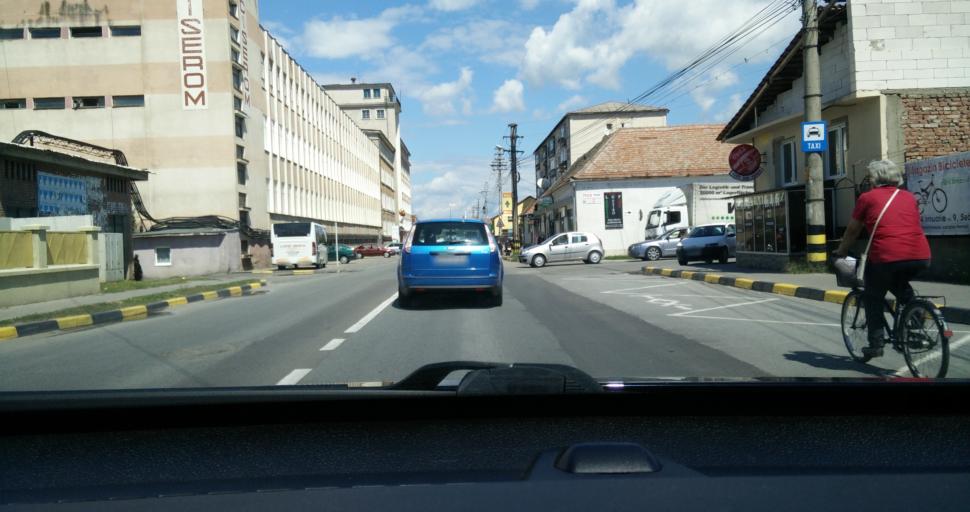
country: RO
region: Alba
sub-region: Municipiul Sebes
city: Sebes
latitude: 45.9499
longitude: 23.5656
